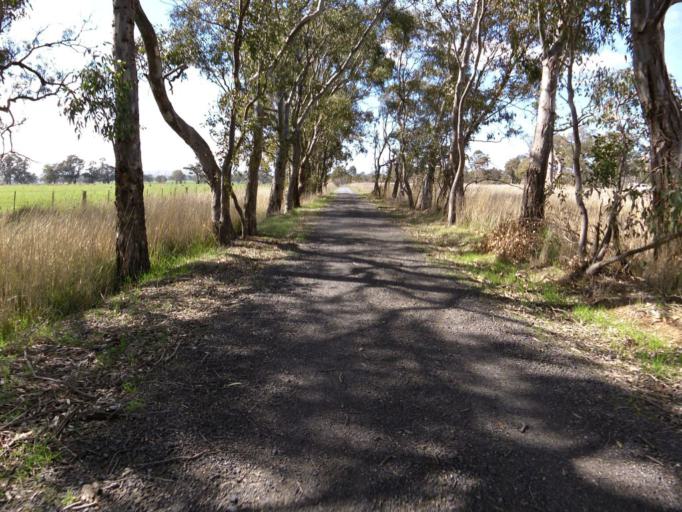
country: AU
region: Victoria
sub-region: Mansfield
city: Mansfield
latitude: -37.0432
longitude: 146.0401
